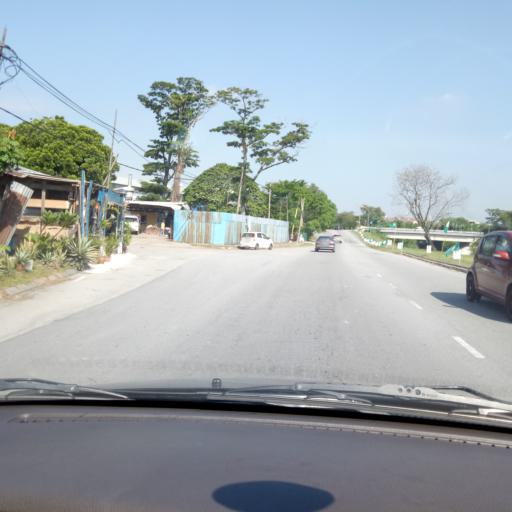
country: MY
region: Selangor
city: Kampong Baharu Balakong
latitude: 3.0155
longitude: 101.7650
